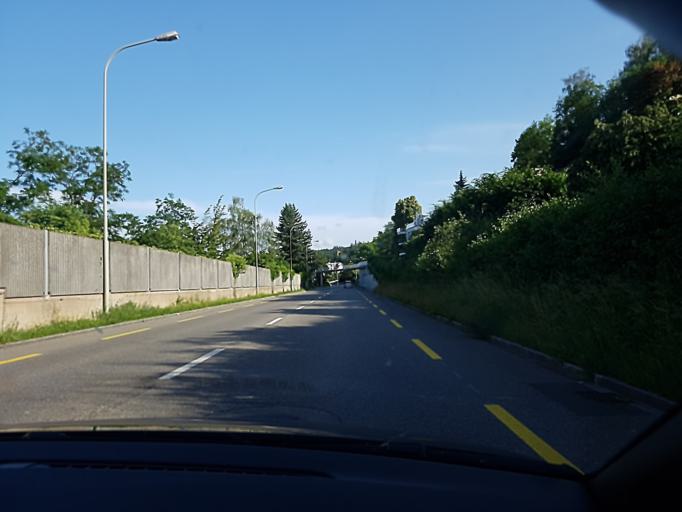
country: CH
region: Zurich
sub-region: Bezirk Horgen
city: Thalwil / Nord
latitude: 47.2954
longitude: 8.5556
